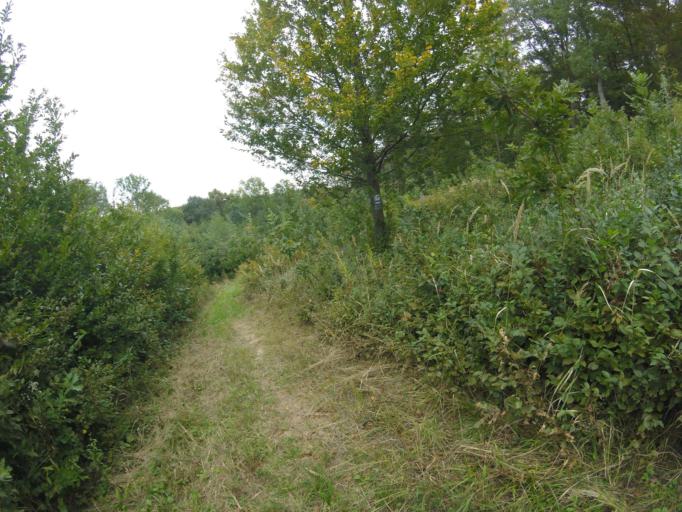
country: HU
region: Vas
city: Csepreg
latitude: 47.3585
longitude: 16.6593
